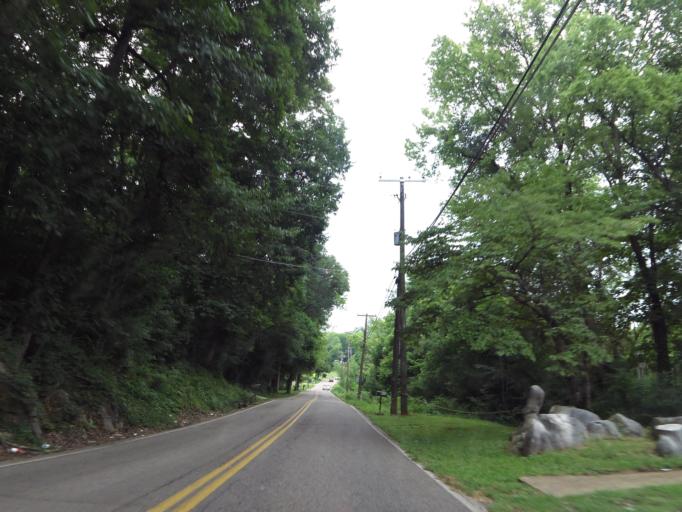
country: US
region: Tennessee
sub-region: Knox County
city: Knoxville
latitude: 35.9421
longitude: -83.8796
